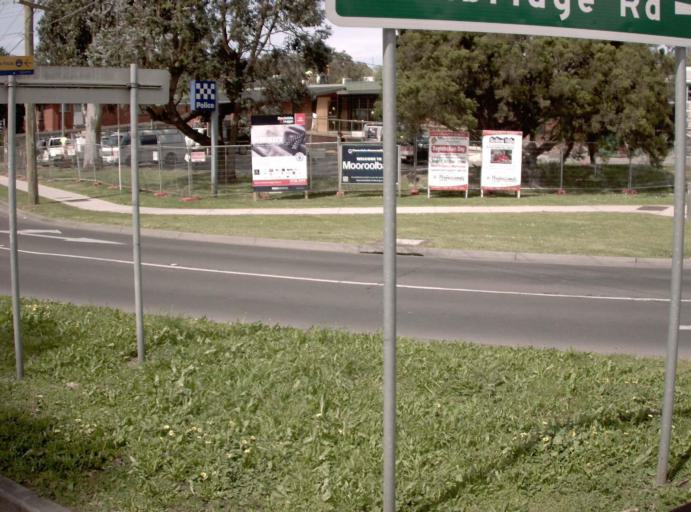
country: AU
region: Victoria
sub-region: Maroondah
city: Croydon North
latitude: -37.7894
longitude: 145.3101
